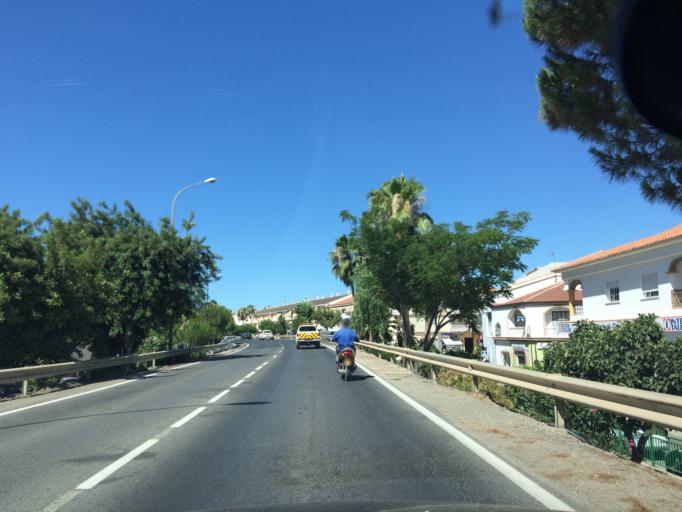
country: ES
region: Andalusia
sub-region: Provincia de Malaga
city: Estacion de Cartama
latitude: 36.7362
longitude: -4.6103
